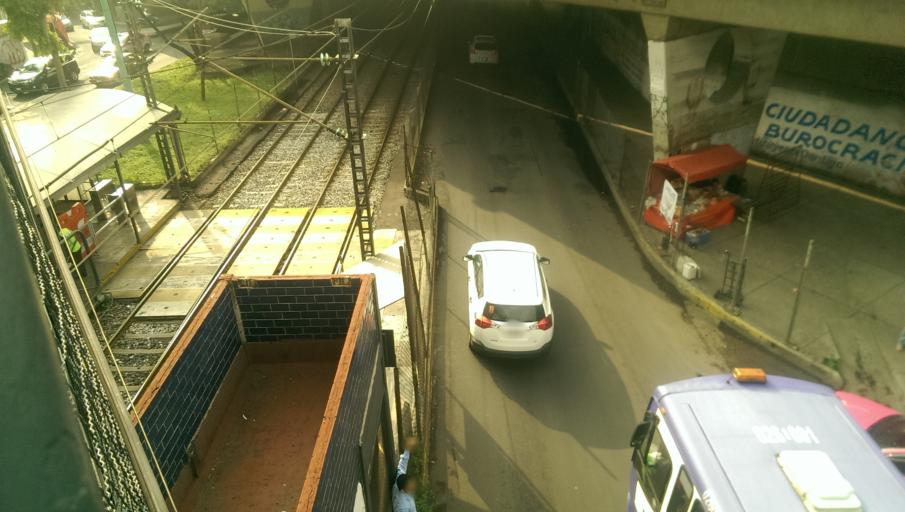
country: MX
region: Mexico City
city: Tlalpan
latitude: 19.2826
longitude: -99.1396
